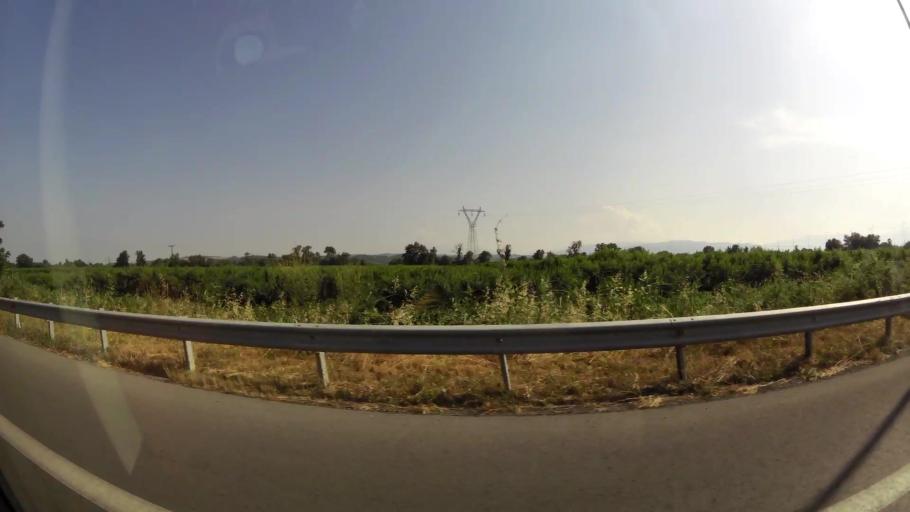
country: GR
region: Central Macedonia
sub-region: Nomos Imathias
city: Agkathia
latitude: 40.5866
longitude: 22.4747
